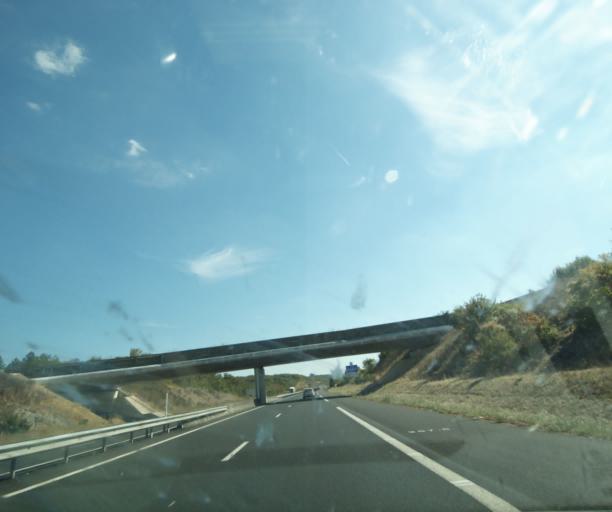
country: FR
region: Limousin
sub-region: Departement de la Correze
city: Brive-la-Gaillarde
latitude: 45.0457
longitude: 1.5178
